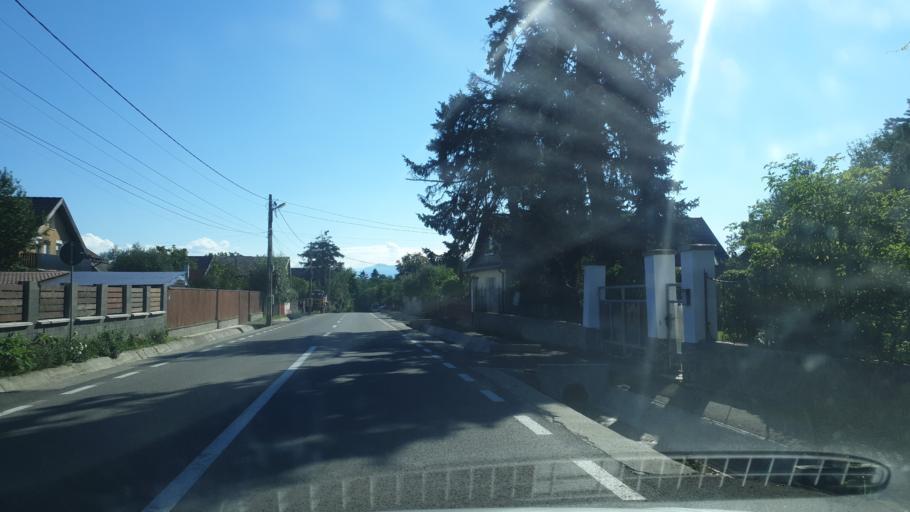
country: RO
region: Covasna
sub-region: Comuna Ilieni
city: Ilieni
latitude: 45.7787
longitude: 25.7540
